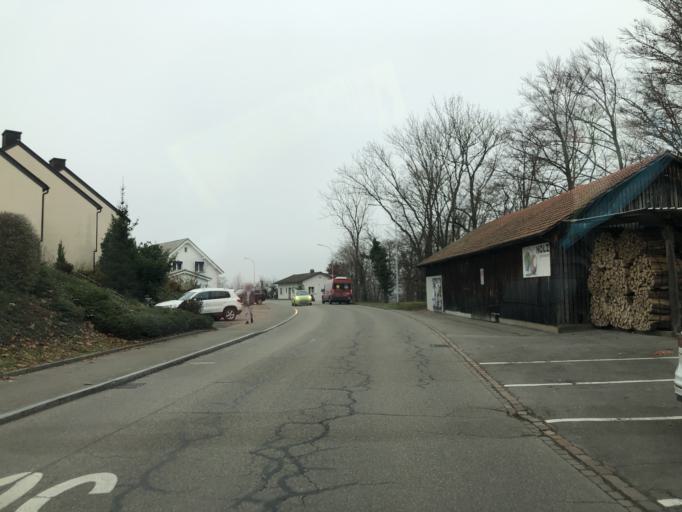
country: CH
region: Aargau
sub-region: Bezirk Baden
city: Gebenstorf
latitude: 47.4798
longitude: 8.2392
